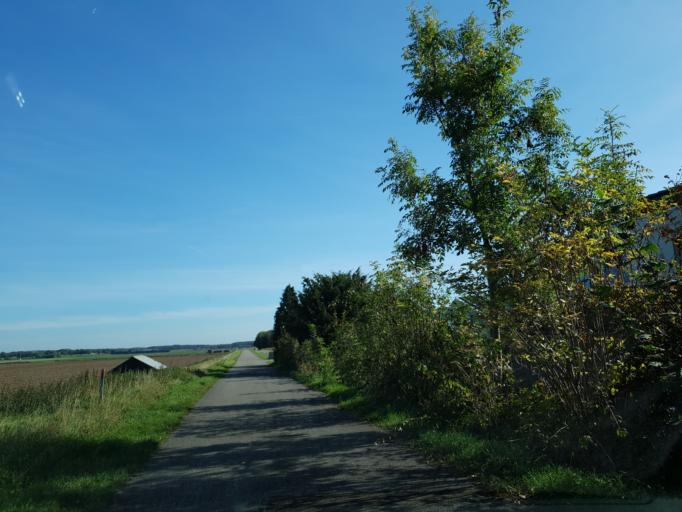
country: NL
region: North Brabant
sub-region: Gemeente Woensdrecht
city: Woensdrecht
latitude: 51.3779
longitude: 4.3070
